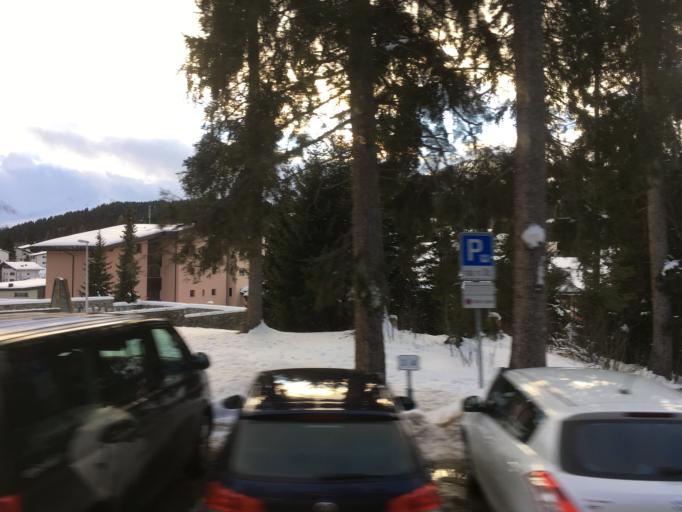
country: CH
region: Grisons
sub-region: Plessur District
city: Churwalden
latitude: 46.7306
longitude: 9.5553
